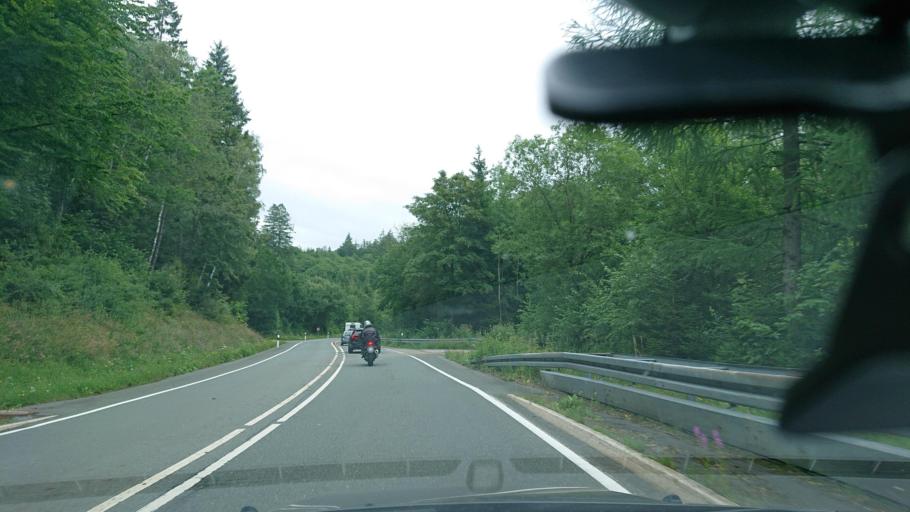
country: DE
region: North Rhine-Westphalia
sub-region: Regierungsbezirk Arnsberg
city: Meschede
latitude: 51.3838
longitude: 8.2895
